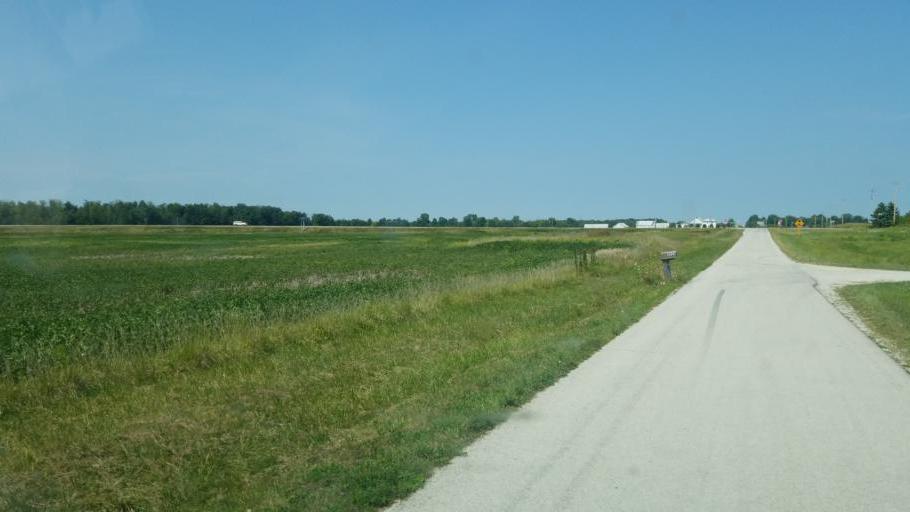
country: US
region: Ohio
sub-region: Crawford County
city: Bucyrus
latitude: 40.8072
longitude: -83.1122
